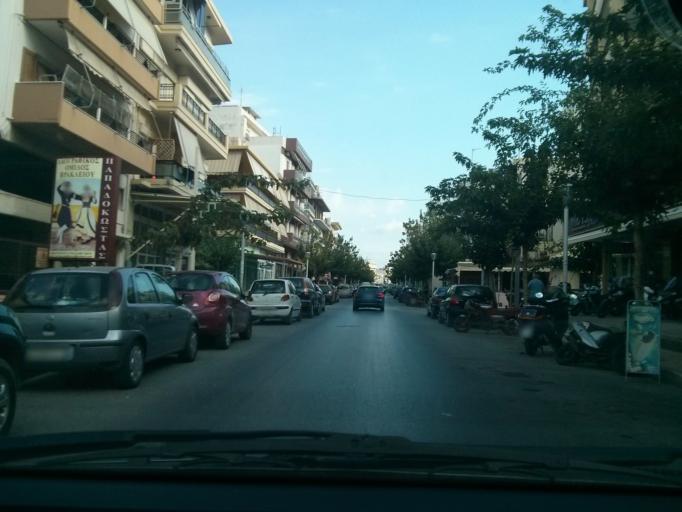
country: GR
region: Crete
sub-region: Nomos Irakleiou
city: Irakleion
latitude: 35.3304
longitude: 25.1362
